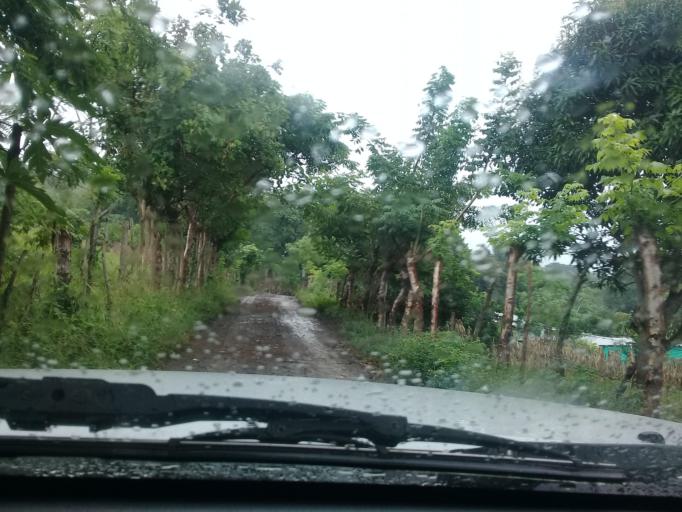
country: MX
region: Veracruz
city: Santiago Tuxtla
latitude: 18.4384
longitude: -95.2951
